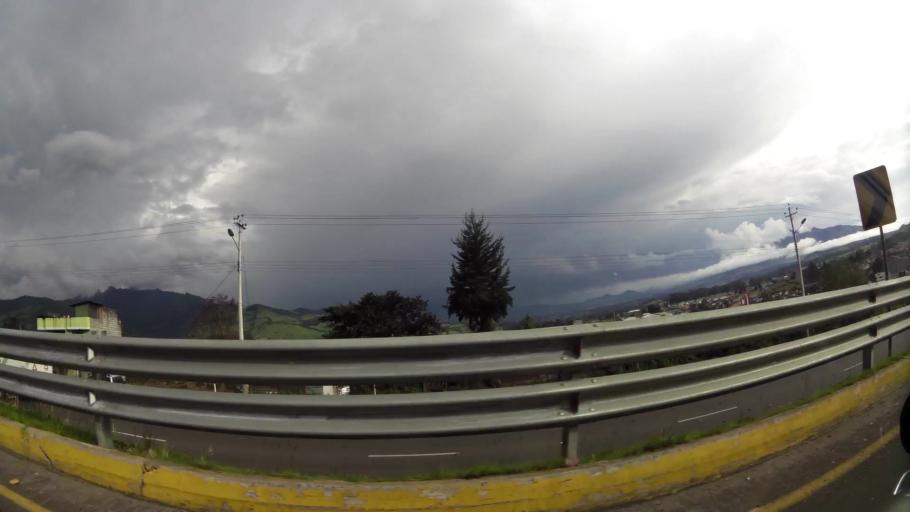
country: EC
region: Pichincha
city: Machachi
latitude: -0.4012
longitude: -78.5429
